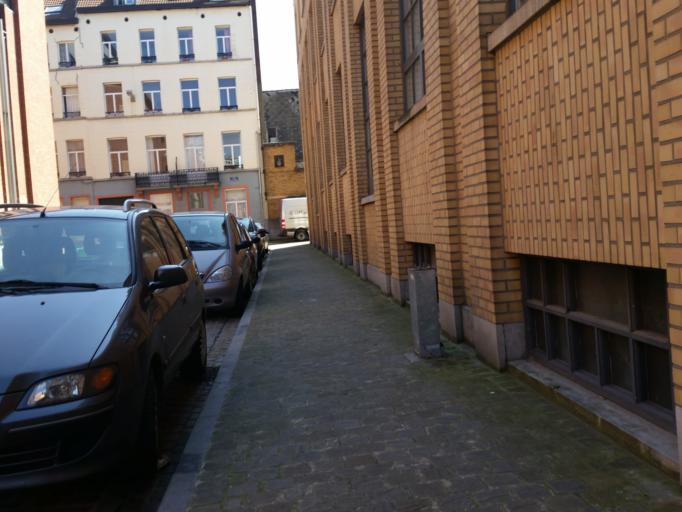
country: BE
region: Brussels Capital
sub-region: Bruxelles-Capitale
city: Brussels
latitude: 50.8567
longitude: 4.3496
